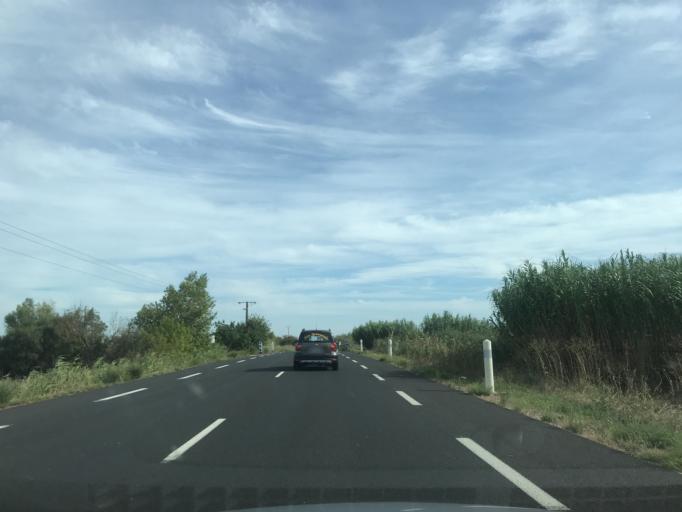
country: FR
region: Languedoc-Roussillon
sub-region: Departement du Gard
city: Aigues-Mortes
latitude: 43.5591
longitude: 4.3182
